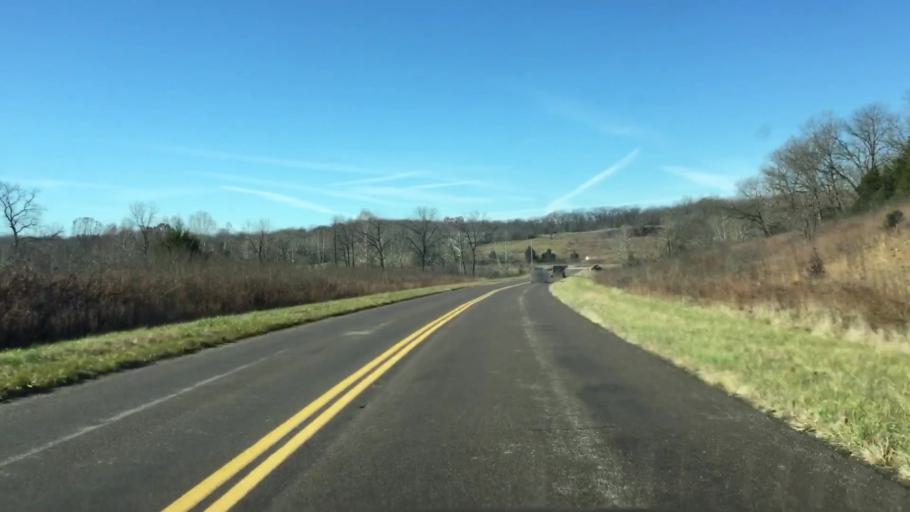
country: US
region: Missouri
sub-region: Miller County
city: Eldon
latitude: 38.3386
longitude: -92.7165
